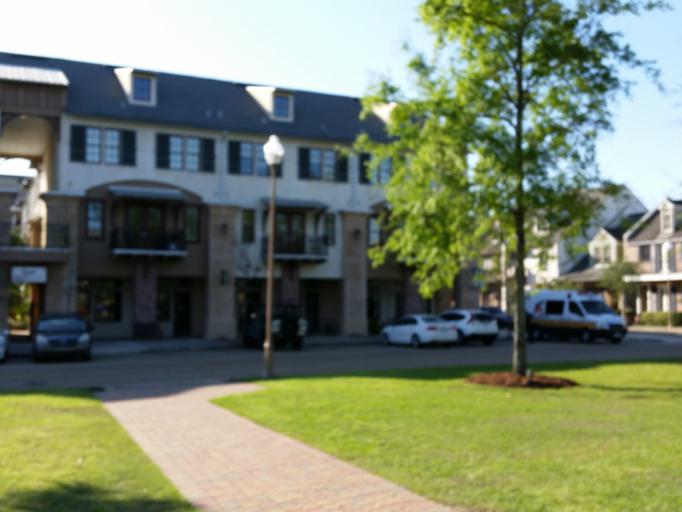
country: US
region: Louisiana
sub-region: Lafayette Parish
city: Lafayette
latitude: 30.1730
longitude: -92.0419
